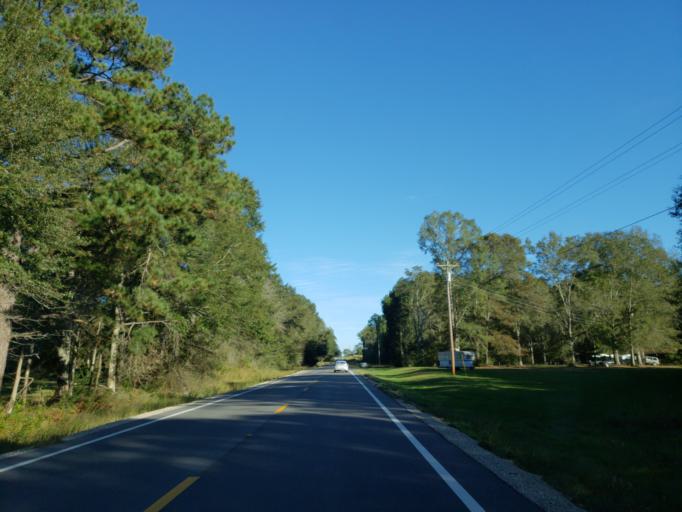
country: US
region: Mississippi
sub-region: Perry County
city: Richton
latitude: 31.3624
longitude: -89.0469
